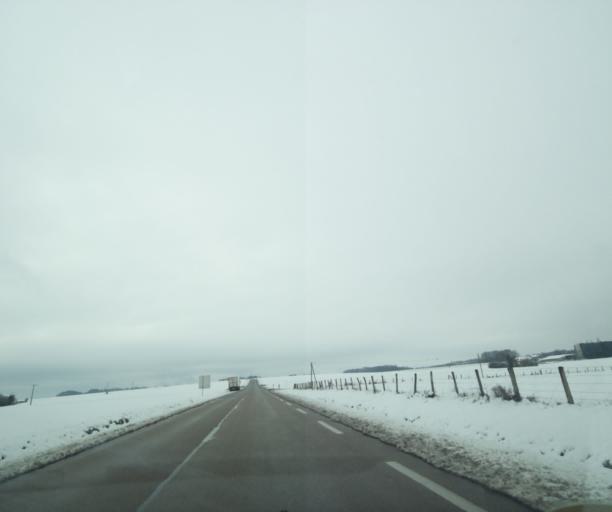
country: FR
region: Champagne-Ardenne
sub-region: Departement de la Haute-Marne
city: Montier-en-Der
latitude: 48.4622
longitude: 4.7572
